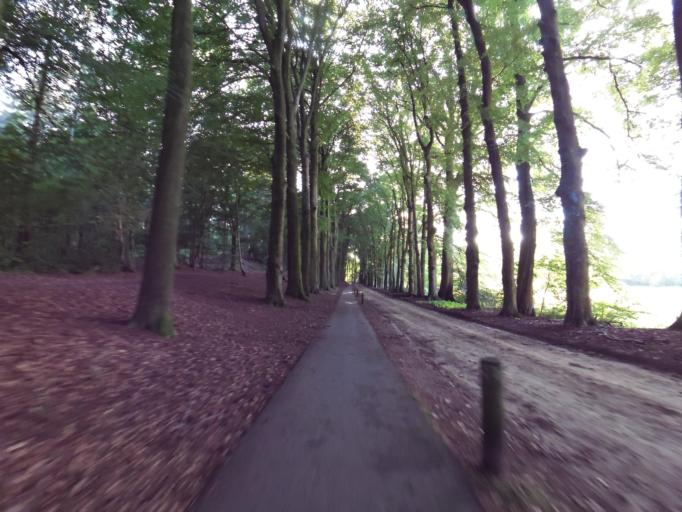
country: NL
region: Gelderland
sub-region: Gemeente Bronckhorst
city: Baak
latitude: 52.0009
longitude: 6.2192
